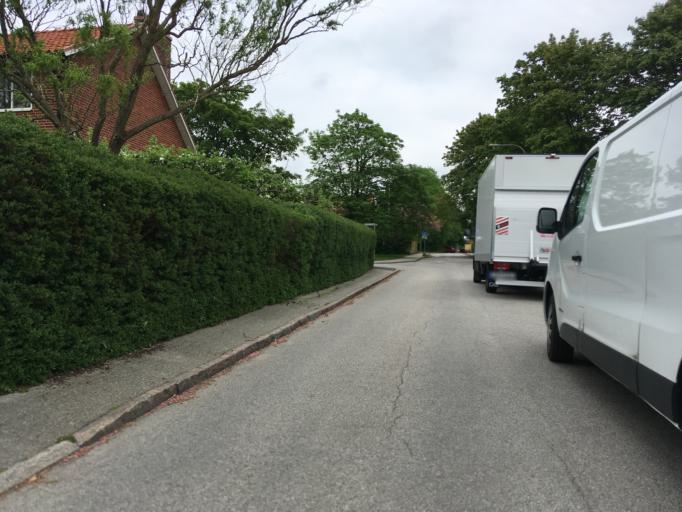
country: SE
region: Skane
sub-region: Lunds Kommun
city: Lund
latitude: 55.7001
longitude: 13.1691
